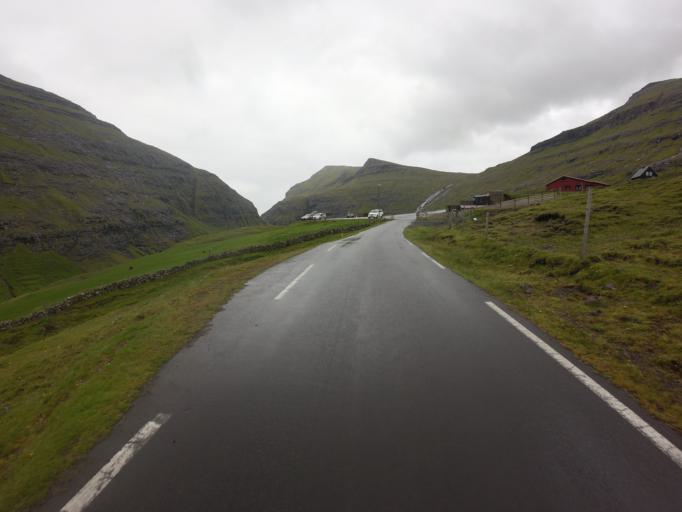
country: FO
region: Streymoy
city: Vestmanna
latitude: 62.2456
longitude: -7.1756
